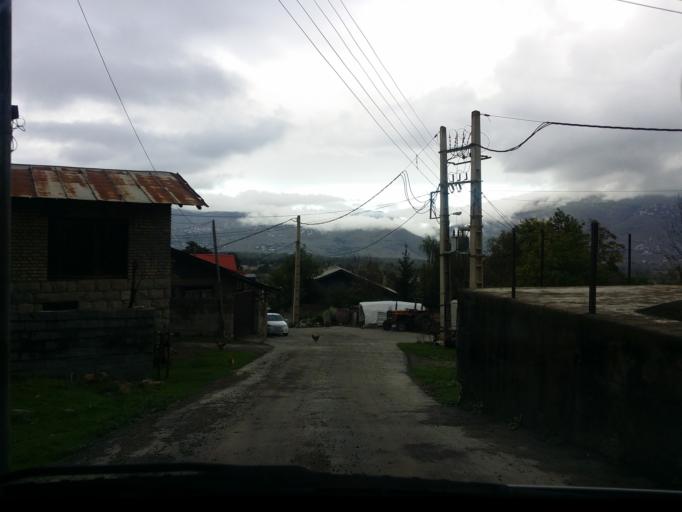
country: IR
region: Mazandaran
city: `Abbasabad
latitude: 36.5035
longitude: 51.1902
